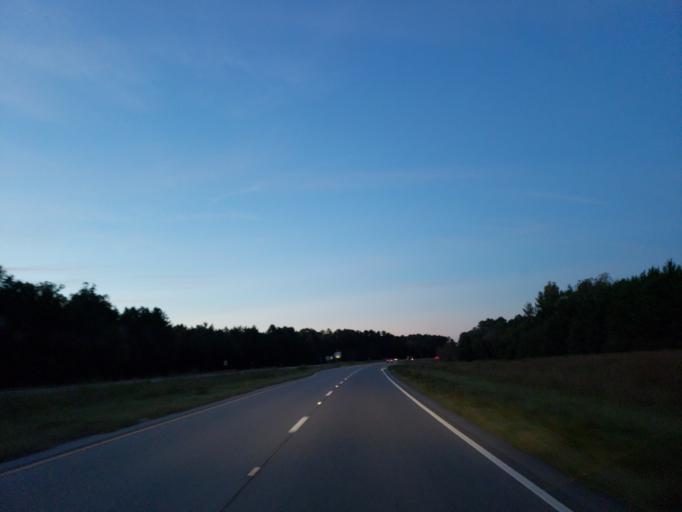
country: US
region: Mississippi
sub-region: Clarke County
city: Quitman
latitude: 31.8535
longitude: -88.7192
